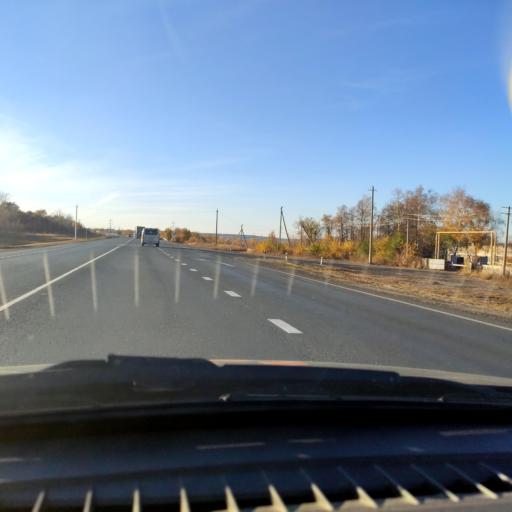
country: RU
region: Samara
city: Varlamovo
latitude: 53.1925
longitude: 48.3373
